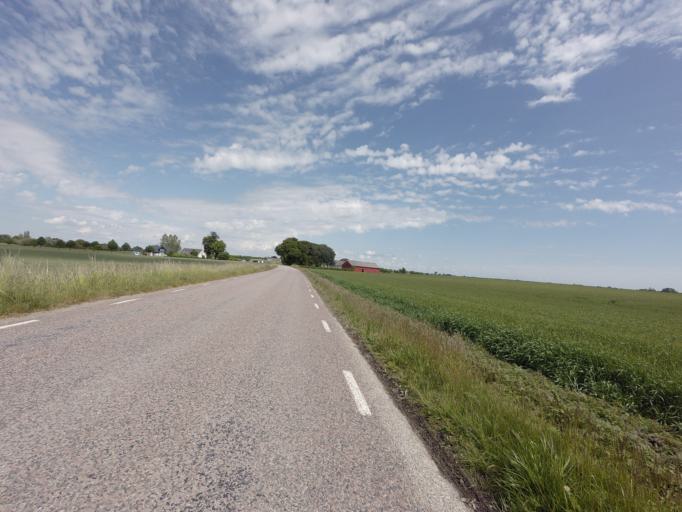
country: SE
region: Skane
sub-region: Vellinge Kommun
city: Vellinge
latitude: 55.4418
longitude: 13.0756
